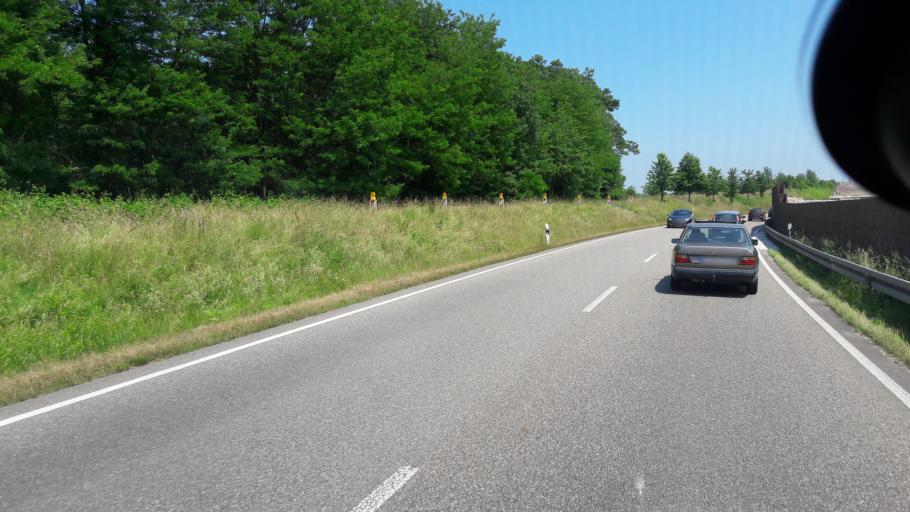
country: DE
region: Baden-Wuerttemberg
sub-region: Karlsruhe Region
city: Otigheim
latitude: 48.8747
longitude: 8.2382
